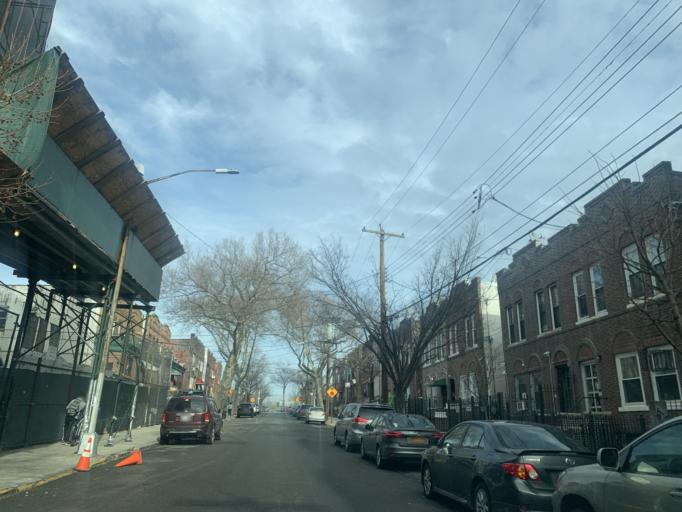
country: US
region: New York
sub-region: Queens County
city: Long Island City
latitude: 40.7066
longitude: -73.9193
